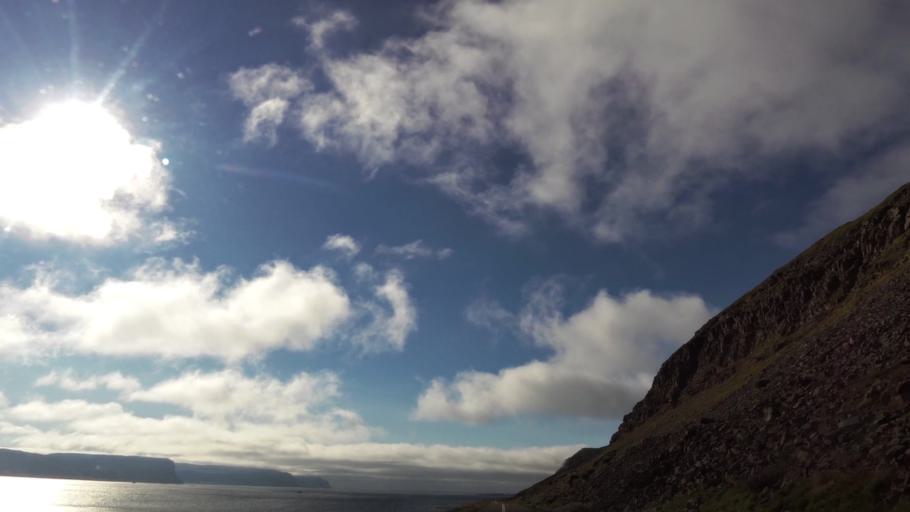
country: IS
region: West
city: Olafsvik
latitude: 65.5693
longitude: -23.9293
